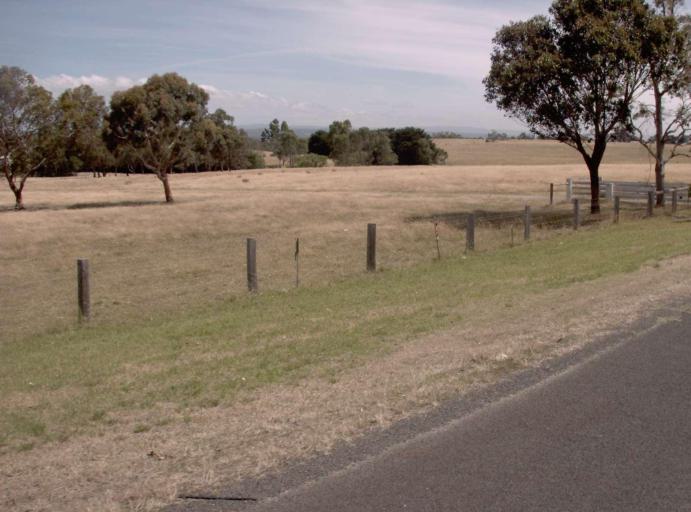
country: AU
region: Victoria
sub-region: Wellington
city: Heyfield
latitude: -38.1328
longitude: 146.8106
